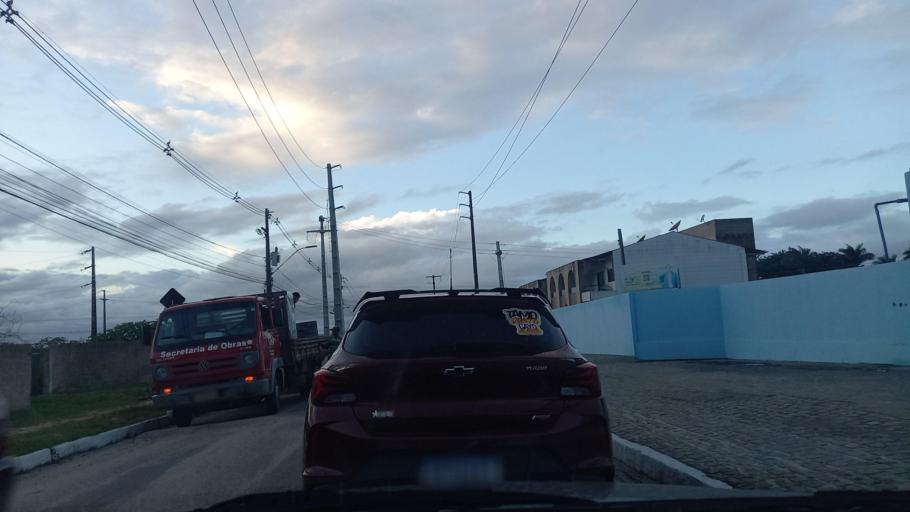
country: BR
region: Pernambuco
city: Garanhuns
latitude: -8.8758
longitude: -36.4654
